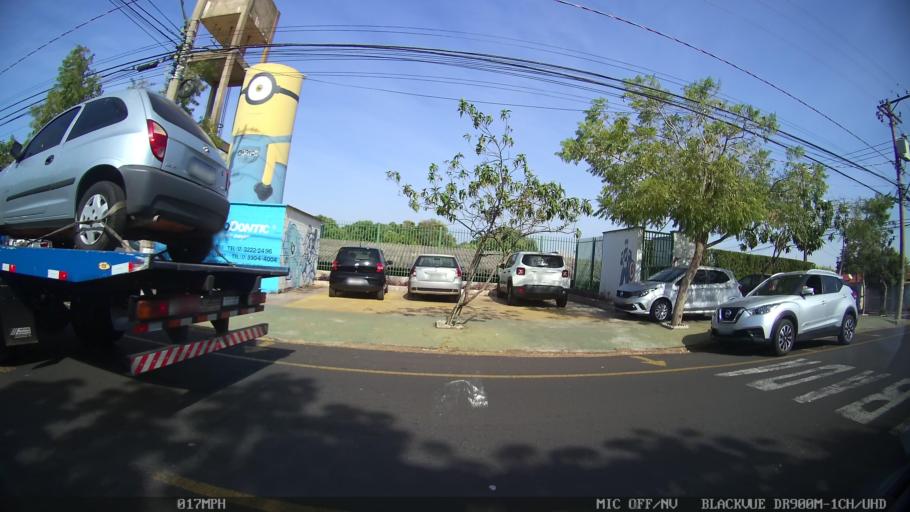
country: BR
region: Sao Paulo
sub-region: Sao Jose Do Rio Preto
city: Sao Jose do Rio Preto
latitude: -20.7960
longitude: -49.4187
